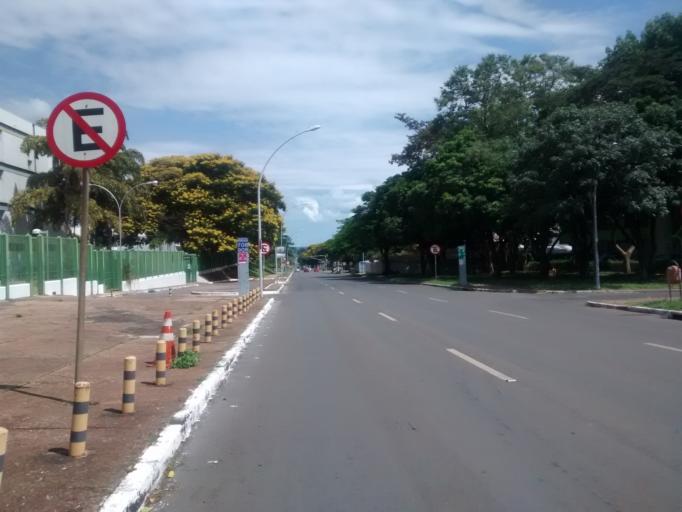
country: BR
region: Federal District
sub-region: Brasilia
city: Brasilia
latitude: -15.7661
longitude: -47.8934
